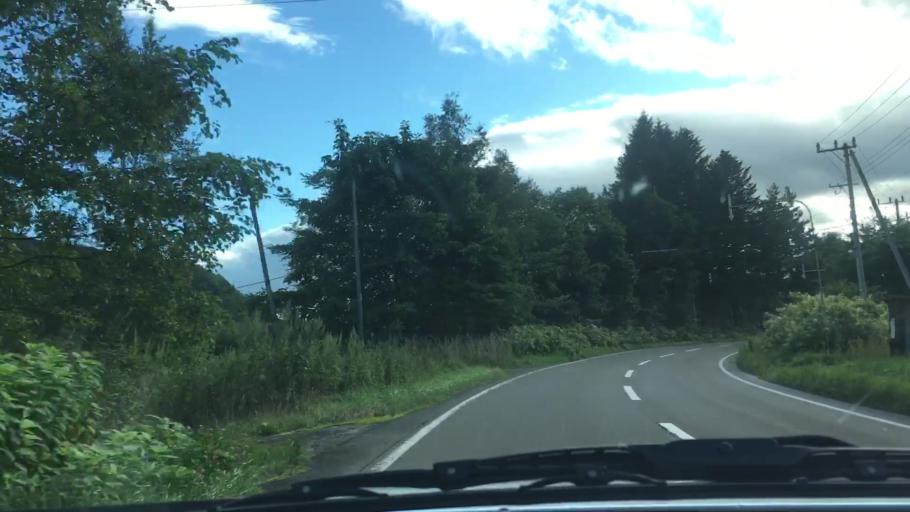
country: JP
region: Hokkaido
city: Otofuke
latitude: 43.1739
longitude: 142.9186
